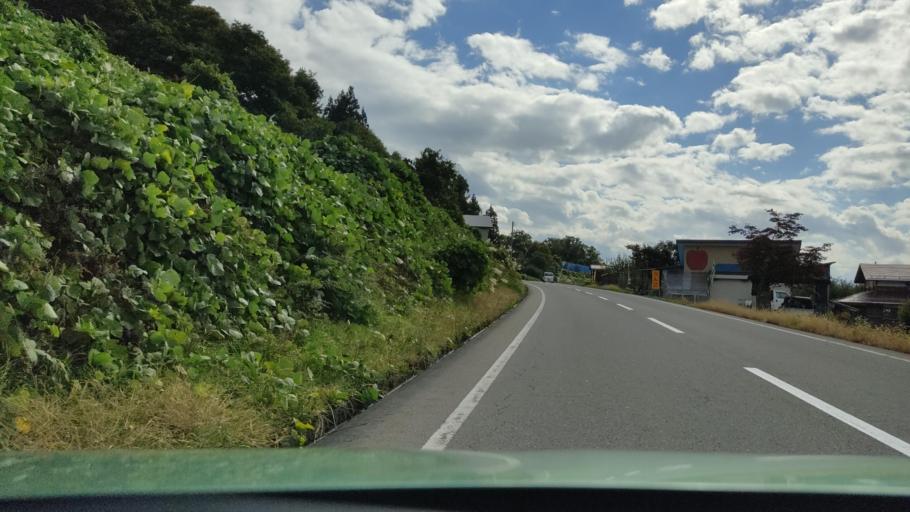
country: JP
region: Akita
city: Yokotemachi
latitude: 39.2301
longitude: 140.5646
